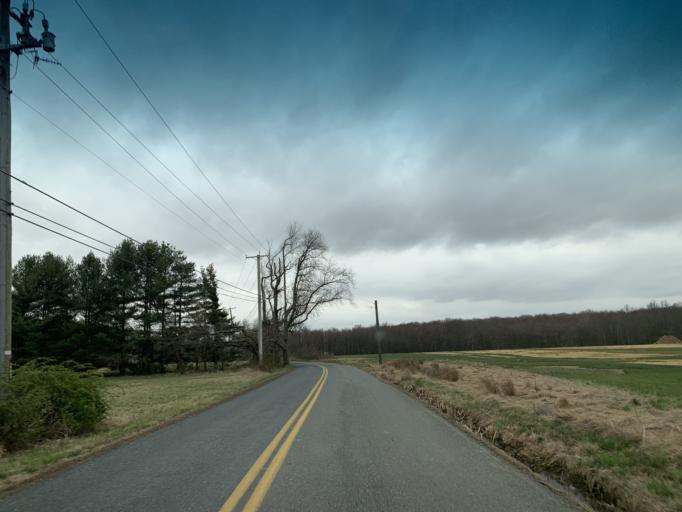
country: US
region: Maryland
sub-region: Harford County
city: Aberdeen
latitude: 39.5614
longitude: -76.1961
